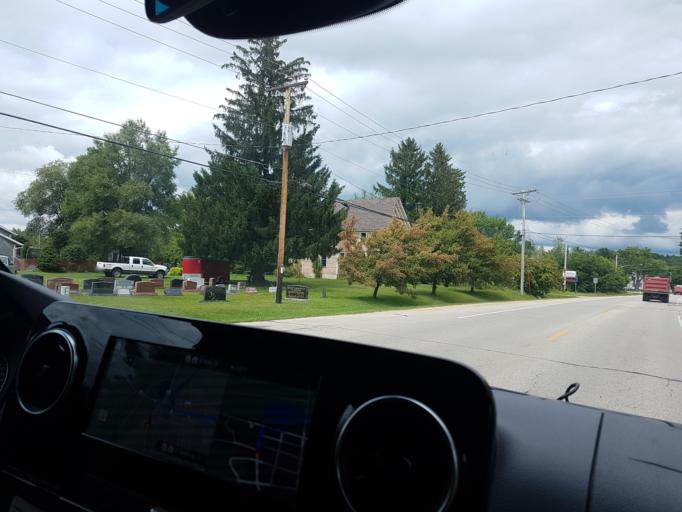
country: US
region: Wisconsin
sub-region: Waushara County
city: Wautoma
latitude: 44.0743
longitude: -89.2969
